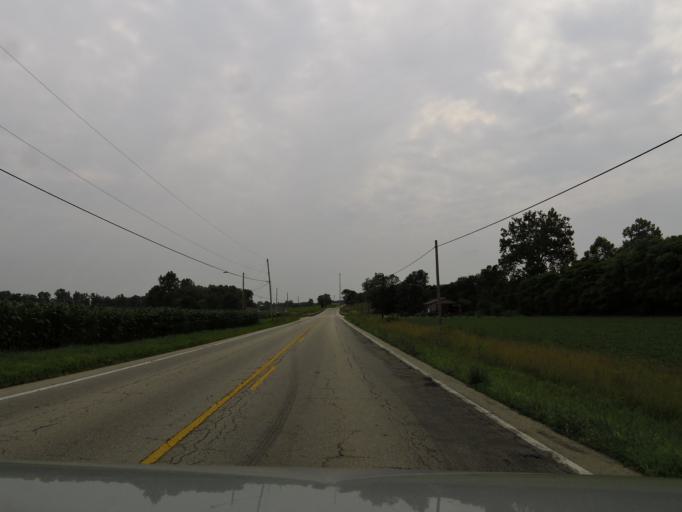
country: US
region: Ohio
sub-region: Clinton County
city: Wilmington
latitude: 39.3515
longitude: -83.8789
